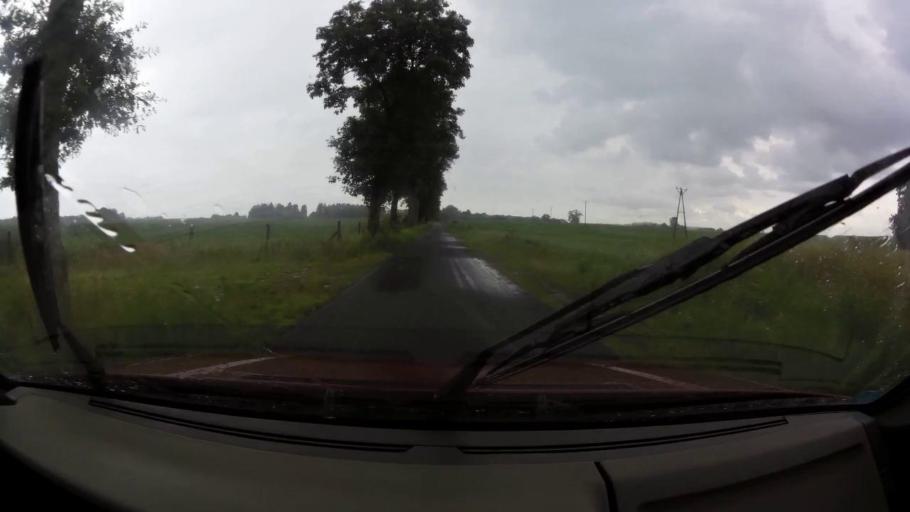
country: PL
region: West Pomeranian Voivodeship
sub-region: Koszalin
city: Koszalin
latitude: 54.0818
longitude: 16.1255
